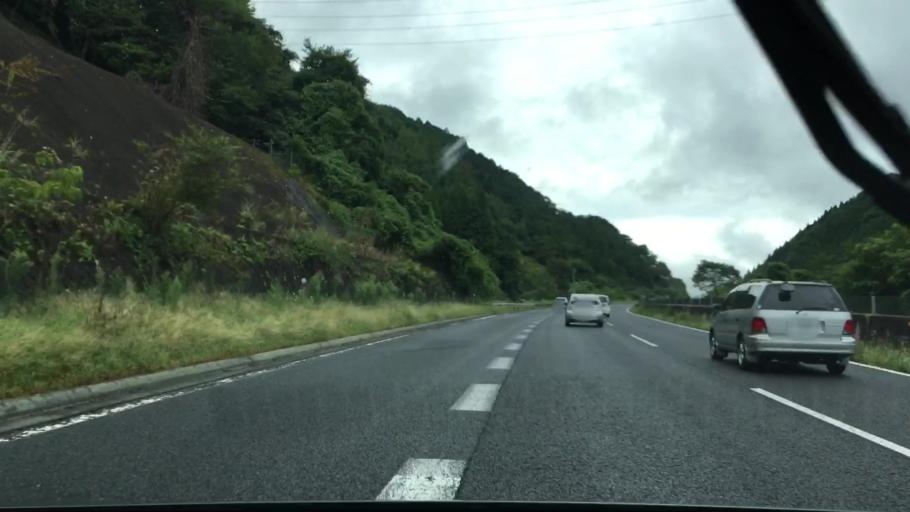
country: JP
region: Hyogo
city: Yamazakicho-nakabirose
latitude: 35.0379
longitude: 134.4729
